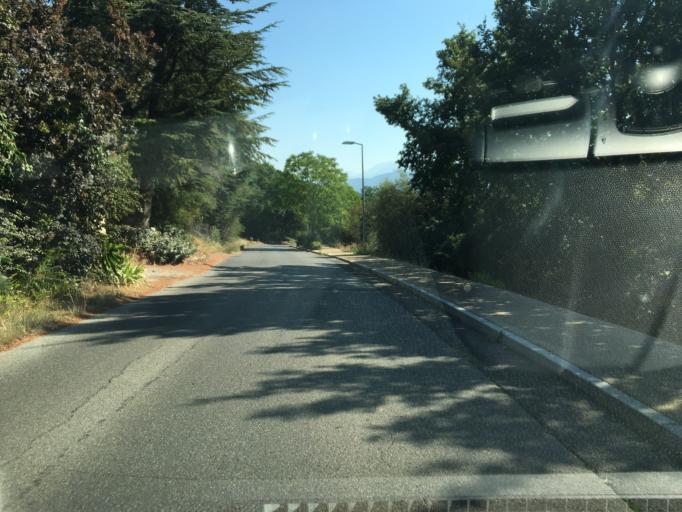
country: FR
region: Provence-Alpes-Cote d'Azur
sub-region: Departement des Alpes-de-Haute-Provence
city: Mallemoisson
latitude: 44.0486
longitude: 6.1370
